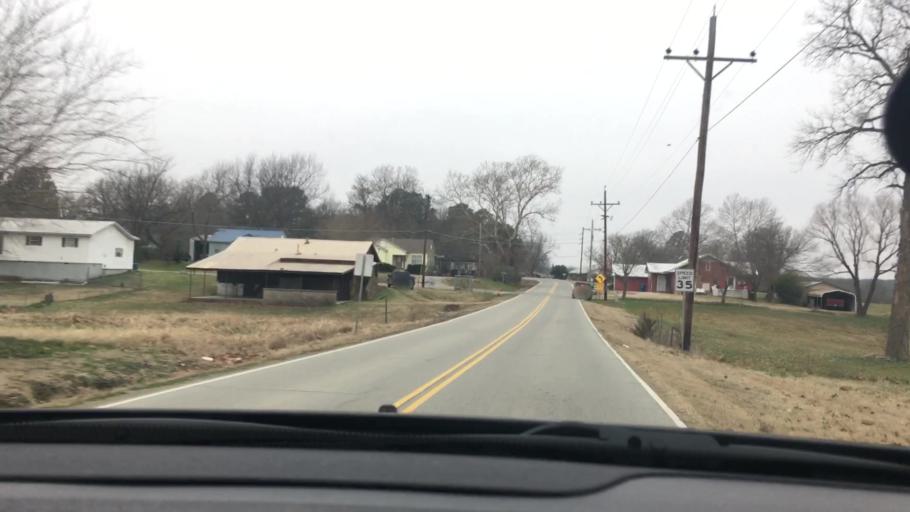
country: US
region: Oklahoma
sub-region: Coal County
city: Coalgate
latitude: 34.5405
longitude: -96.2253
